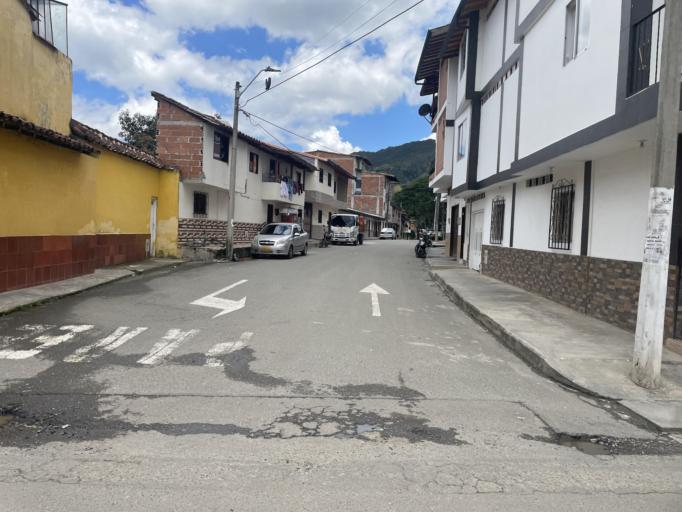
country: CO
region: Antioquia
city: La Ceja
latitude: 6.0233
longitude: -75.4332
